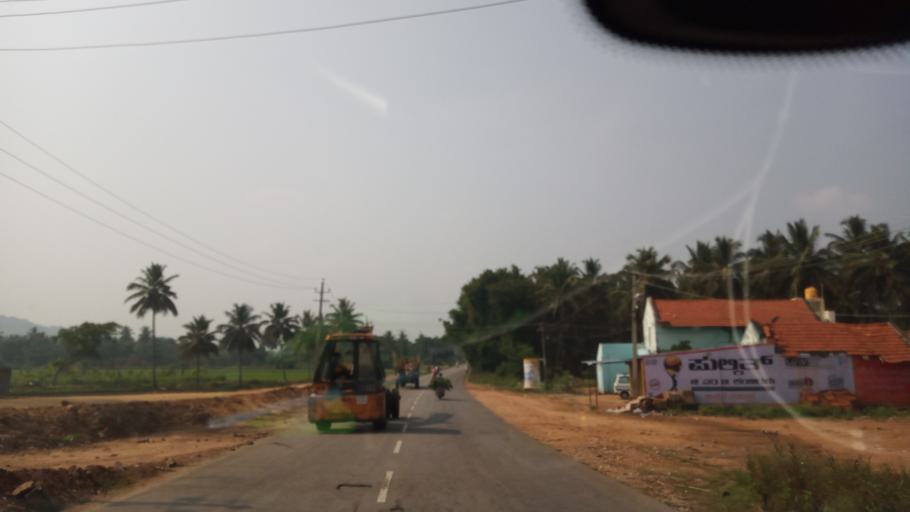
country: IN
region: Karnataka
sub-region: Mandya
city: Pandavapura
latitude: 12.5219
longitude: 76.6729
